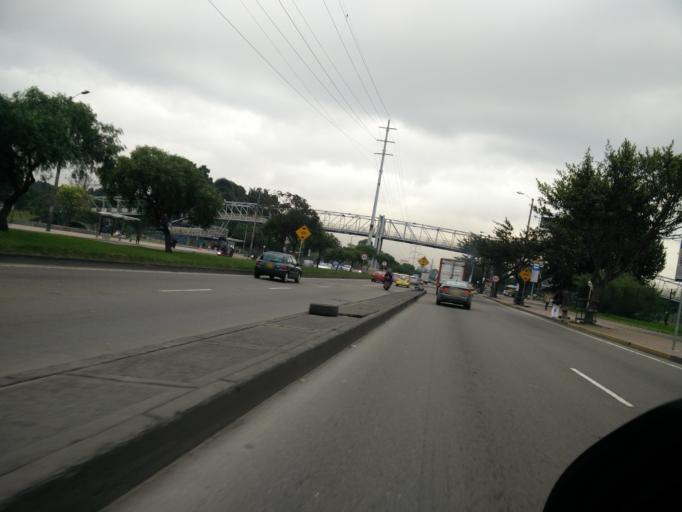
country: CO
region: Bogota D.C.
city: Bogota
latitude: 4.6624
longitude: -74.0967
